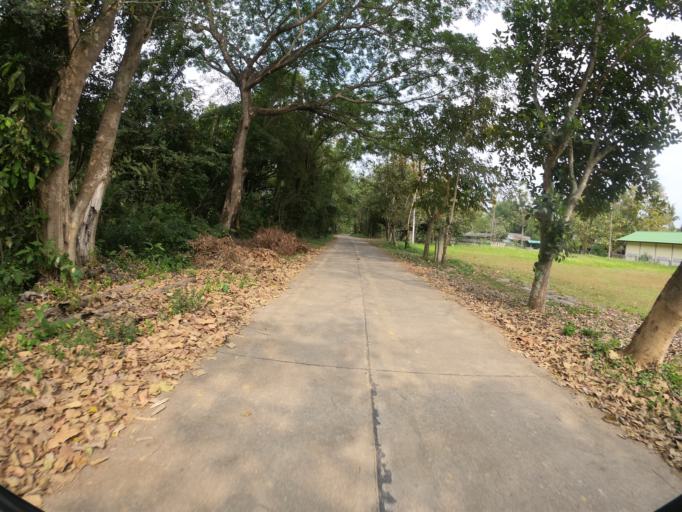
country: TH
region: Chiang Mai
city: Hang Dong
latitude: 18.7382
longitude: 98.9256
